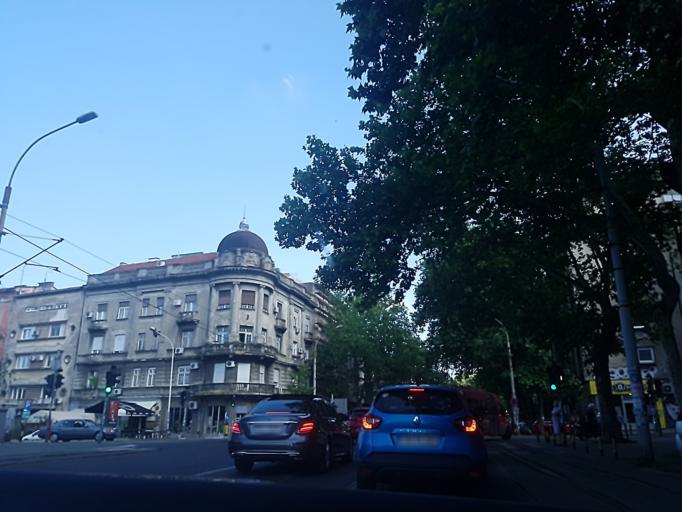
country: RS
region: Central Serbia
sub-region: Belgrade
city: Stari Grad
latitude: 44.8200
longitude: 20.4659
